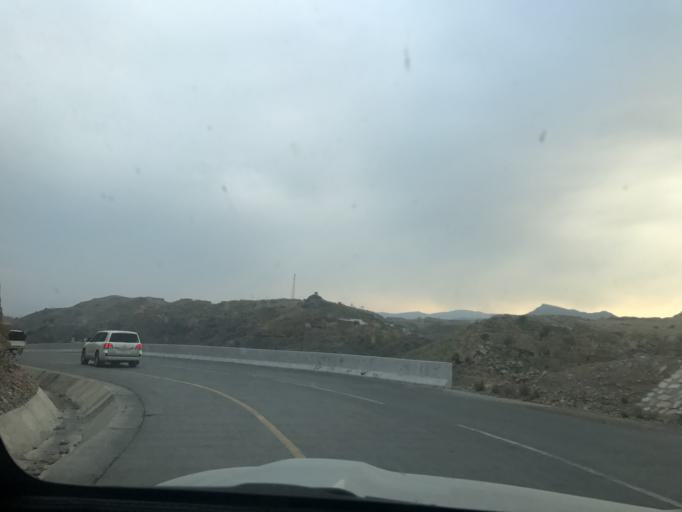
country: PK
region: Federally Administered Tribal Areas
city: Landi Kotal
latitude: 34.0256
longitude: 71.2615
